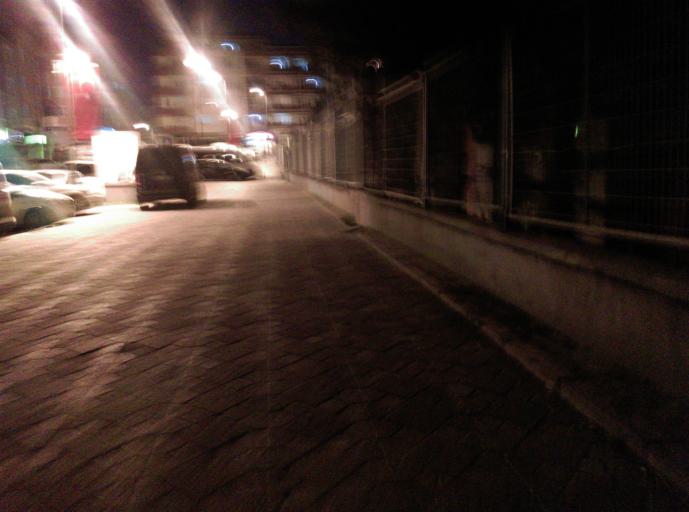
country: TR
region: Istanbul
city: Zeytinburnu
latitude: 41.0099
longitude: 28.9142
